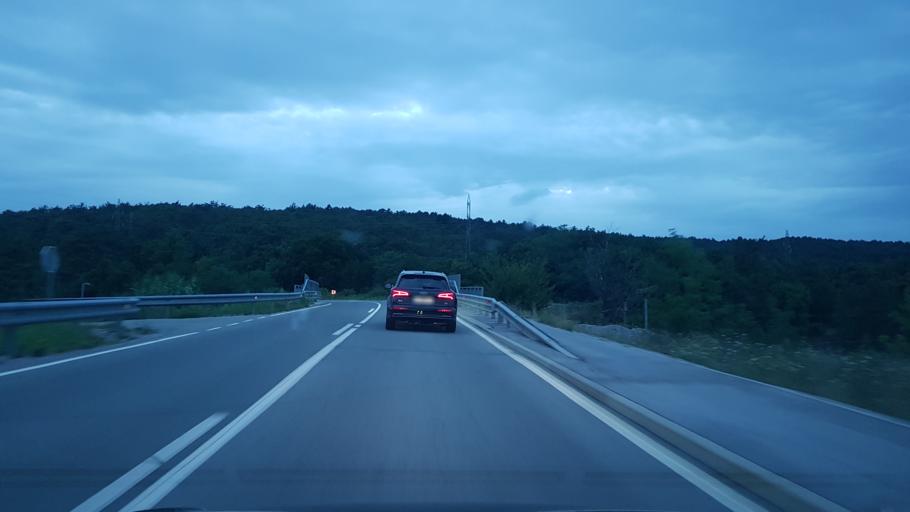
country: SI
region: Divaca
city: Divaca
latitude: 45.6790
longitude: 13.9575
